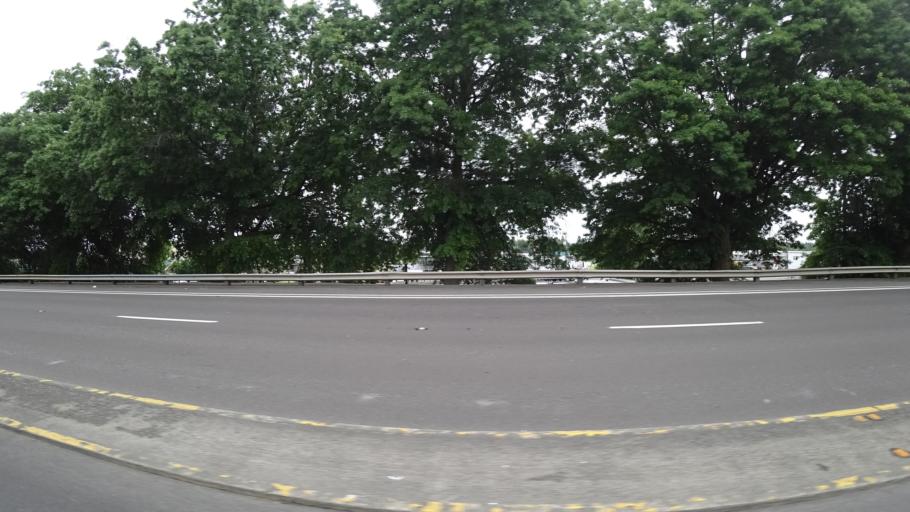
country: US
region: Washington
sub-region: Clark County
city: Vancouver
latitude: 45.5958
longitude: -122.6700
